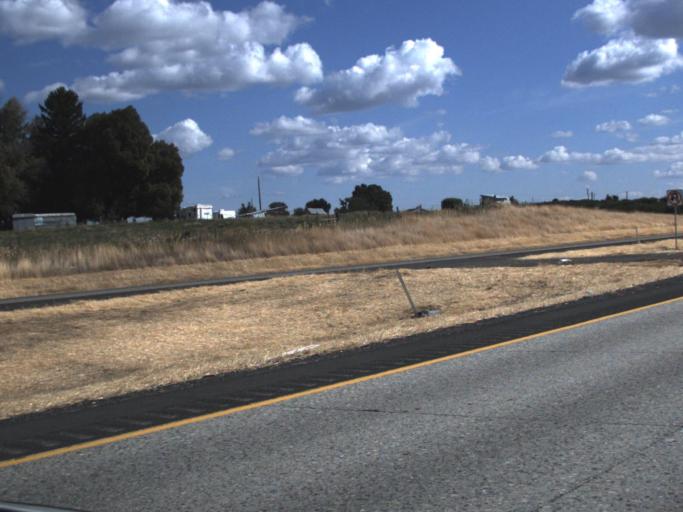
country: US
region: Washington
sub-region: Yakima County
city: Granger
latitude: 46.3705
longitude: -120.2146
